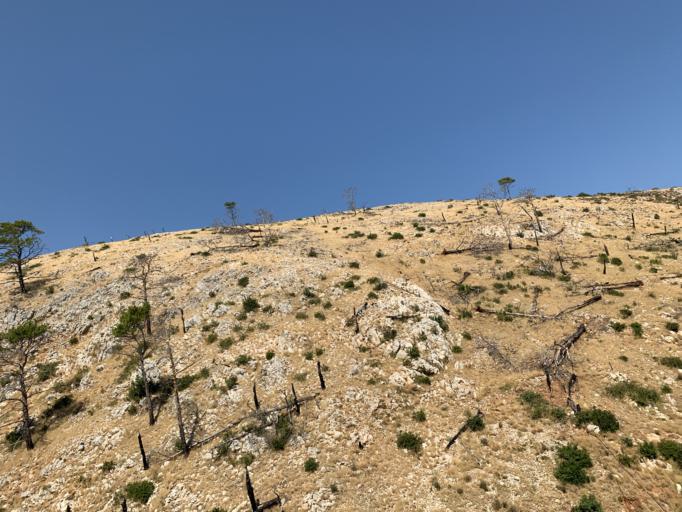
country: GR
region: North Aegean
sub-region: Chios
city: Thymiana
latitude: 38.3152
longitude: 26.0056
